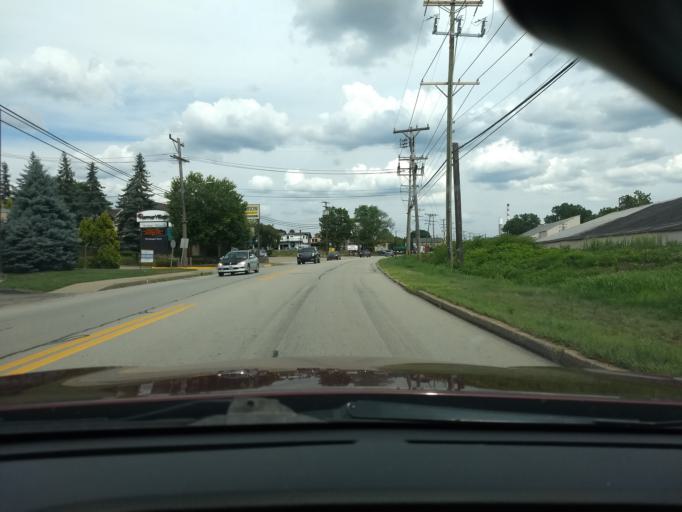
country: US
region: Pennsylvania
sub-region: Allegheny County
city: Cheswick
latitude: 40.5408
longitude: -79.8199
